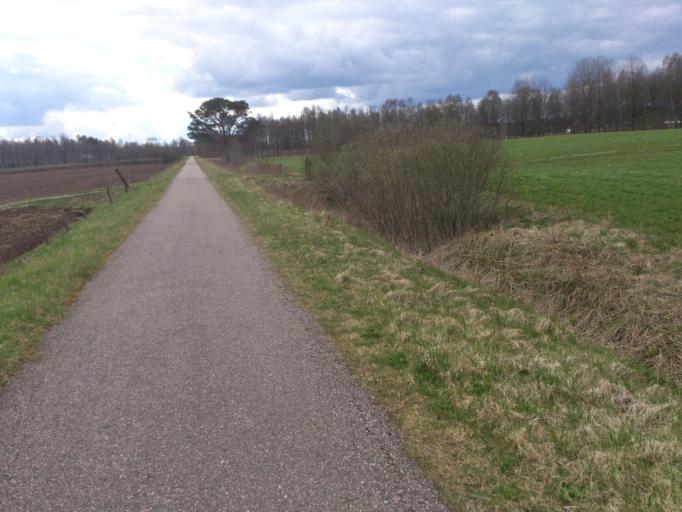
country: SE
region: Vaestra Goetaland
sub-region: Ulricehamns Kommun
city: Ulricehamn
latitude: 57.9600
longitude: 13.5119
